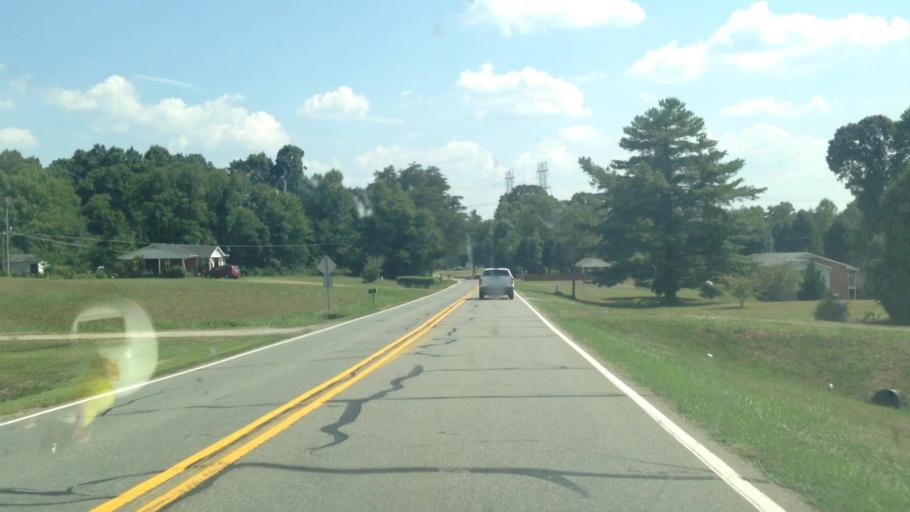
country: US
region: North Carolina
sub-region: Stokes County
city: Walnut Cove
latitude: 36.2772
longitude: -80.0880
